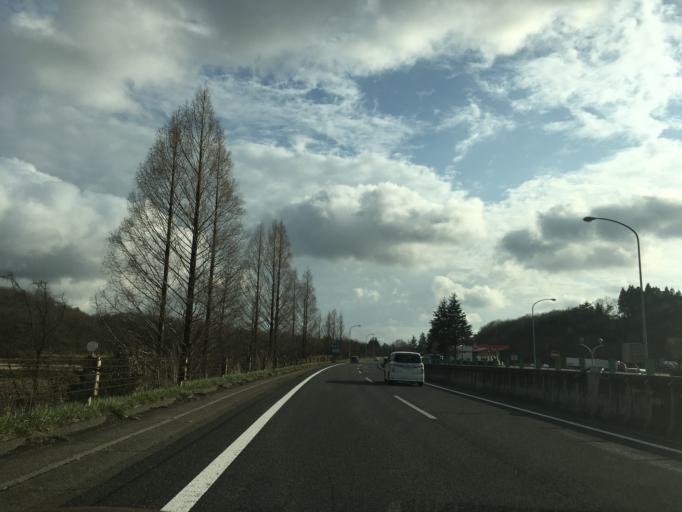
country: JP
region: Miyagi
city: Tomiya
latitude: 38.4138
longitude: 140.9165
